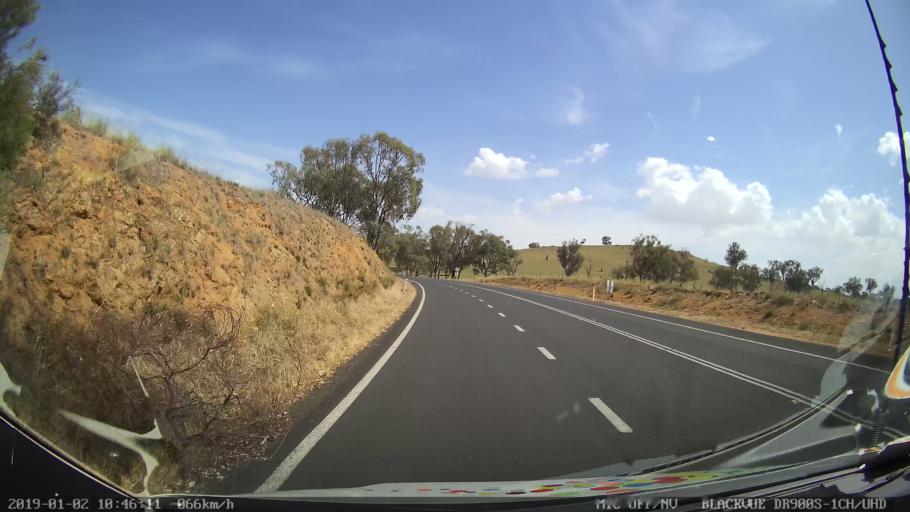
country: AU
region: New South Wales
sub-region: Cootamundra
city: Cootamundra
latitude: -34.7534
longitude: 148.2893
